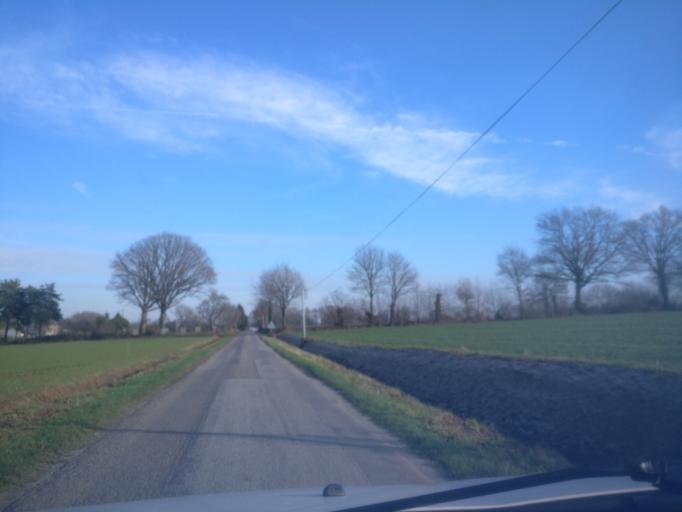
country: FR
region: Brittany
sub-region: Departement d'Ille-et-Vilaine
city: Livre-sur-Changeon
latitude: 48.2110
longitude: -1.2995
